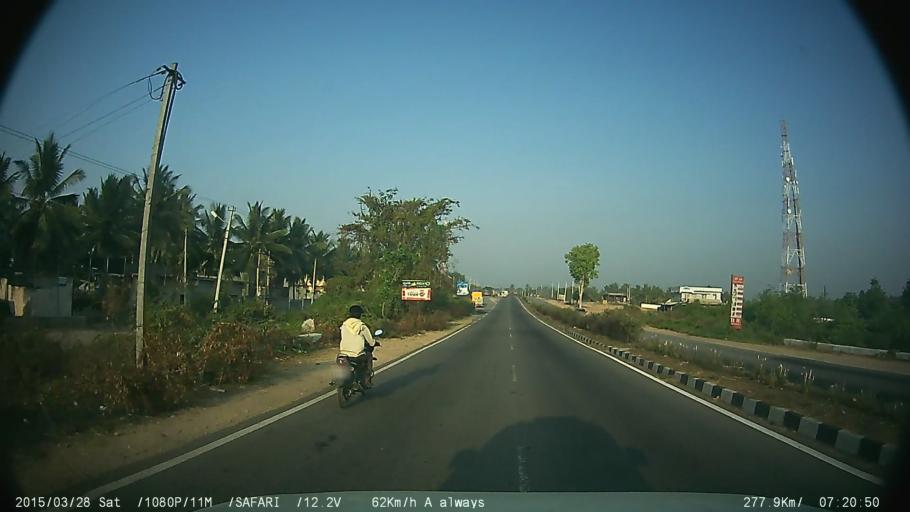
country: IN
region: Karnataka
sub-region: Mandya
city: Mandya
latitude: 12.4966
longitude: 76.8088
